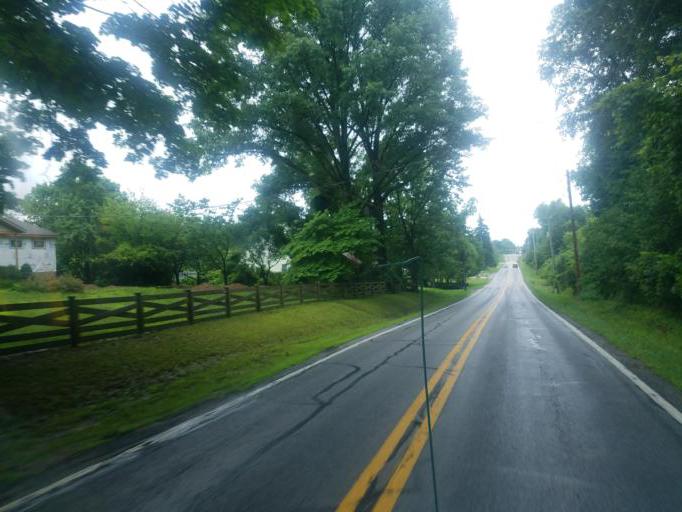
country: US
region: Ohio
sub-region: Franklin County
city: Gahanna
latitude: 40.0081
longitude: -82.8342
